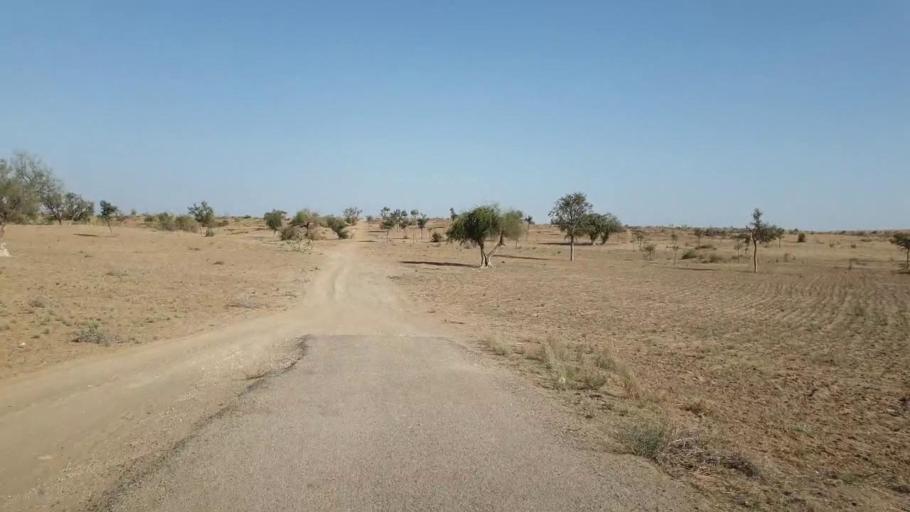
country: PK
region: Sindh
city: Islamkot
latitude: 25.0300
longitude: 70.0422
